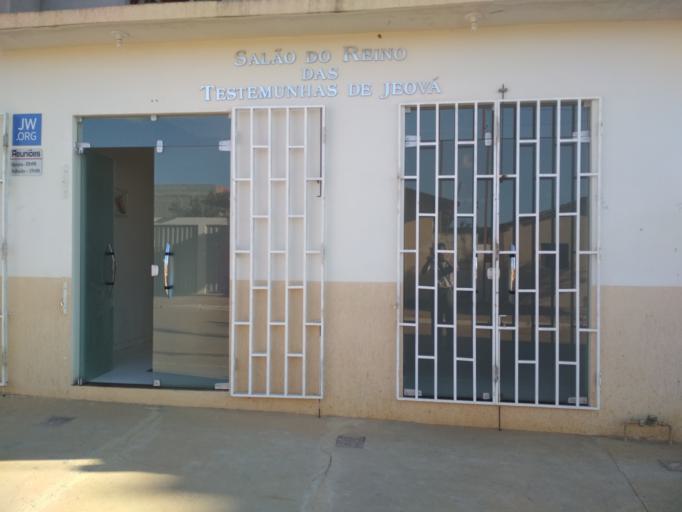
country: BR
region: Bahia
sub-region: Encruzilhada
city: Encruzilhada
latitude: -15.7236
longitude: -41.0018
